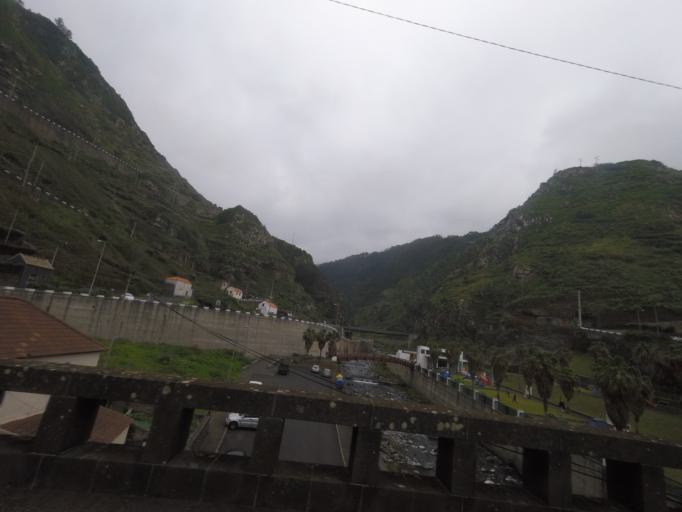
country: PT
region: Madeira
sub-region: Porto Moniz
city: Porto Moniz
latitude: 32.8543
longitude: -17.1542
